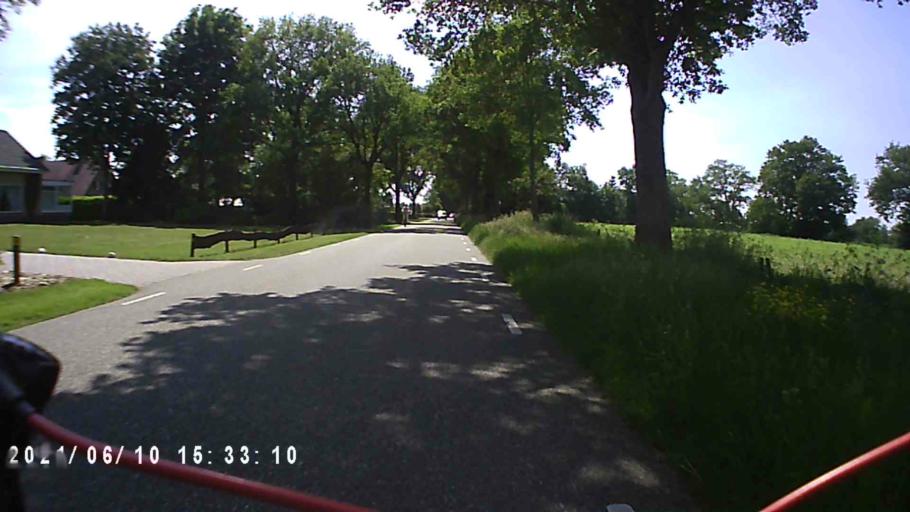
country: NL
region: Friesland
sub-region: Gemeente Achtkarspelen
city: Surhuisterveen
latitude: 53.1692
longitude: 6.1734
